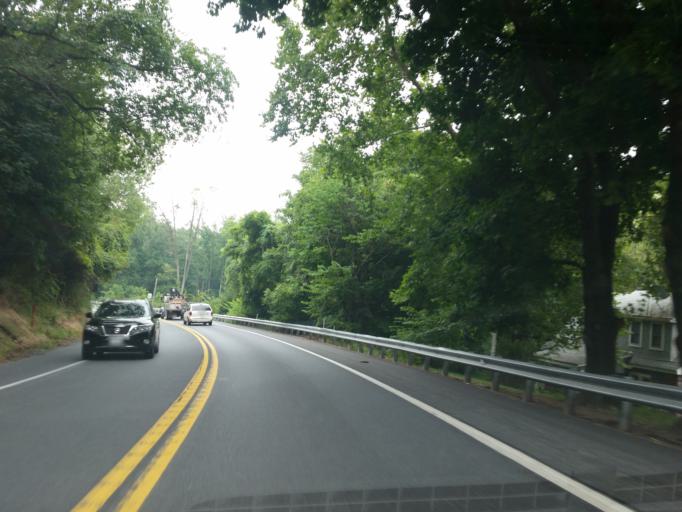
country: US
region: Pennsylvania
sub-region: Lancaster County
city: Brickerville
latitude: 40.2239
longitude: -76.3039
